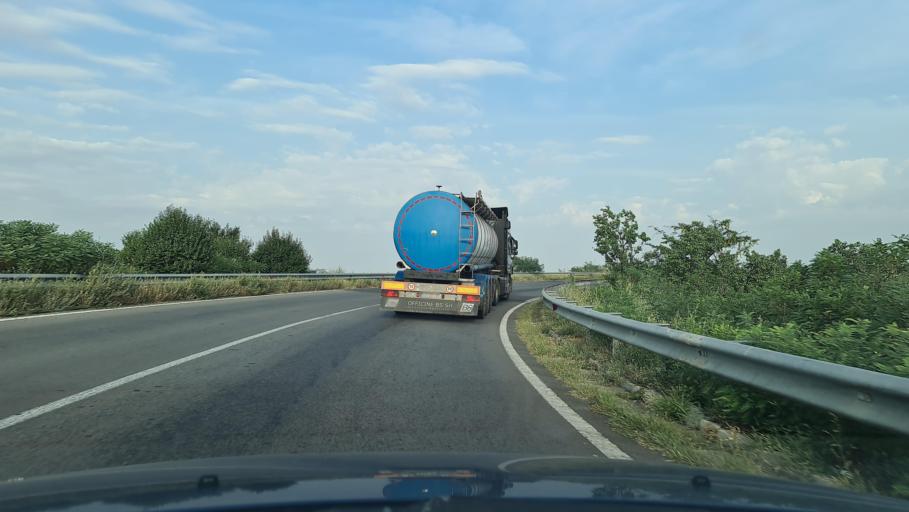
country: RO
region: Calarasi
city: Lehliu-Gara
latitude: 44.4243
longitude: 26.8635
